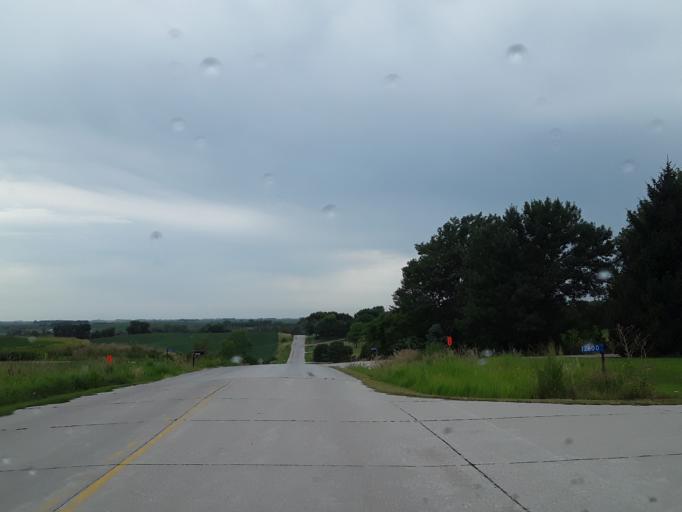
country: US
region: Nebraska
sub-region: Washington County
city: Blair
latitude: 41.5018
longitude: -96.1476
